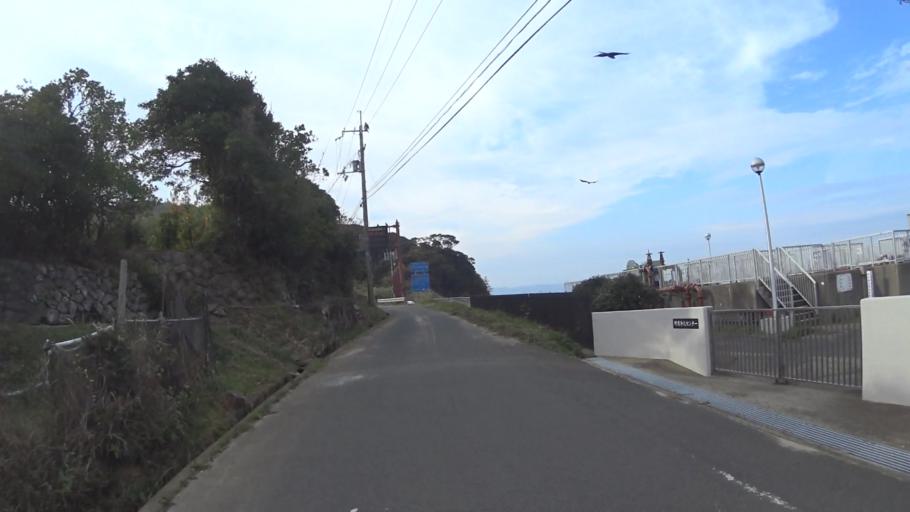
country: JP
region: Kyoto
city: Maizuru
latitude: 35.5663
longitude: 135.4261
